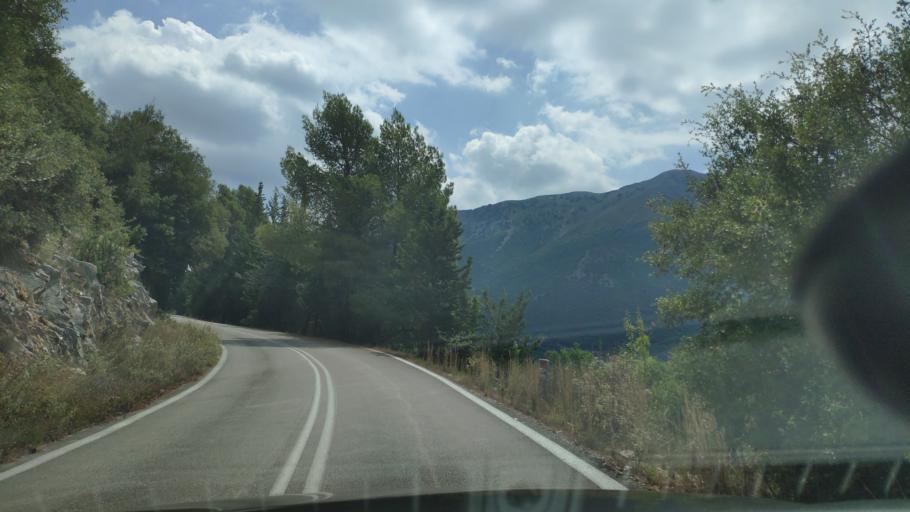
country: GR
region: Epirus
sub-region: Nomos Artas
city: Kampi
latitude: 39.2731
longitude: 20.9324
